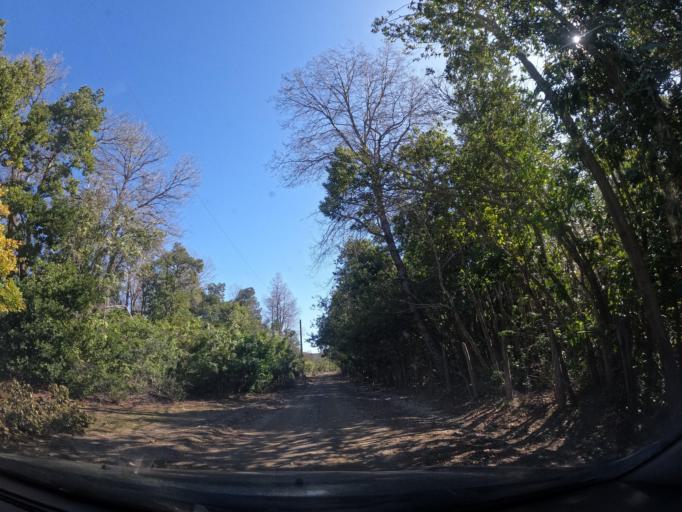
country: CL
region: Maule
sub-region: Provincia de Linares
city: Longavi
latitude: -36.2468
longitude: -71.3404
